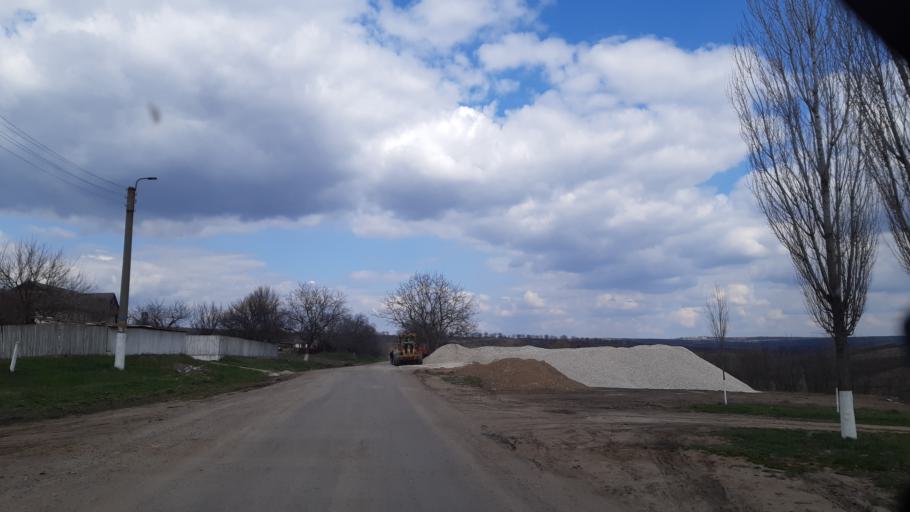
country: MD
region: Laloveni
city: Ialoveni
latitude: 46.8868
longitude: 28.6966
